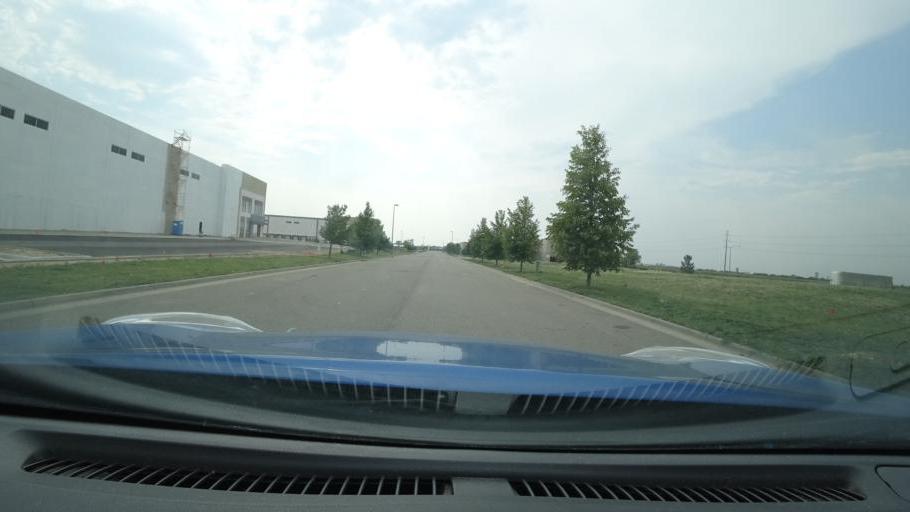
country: US
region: Colorado
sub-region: Adams County
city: Aurora
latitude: 39.7515
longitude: -104.7566
